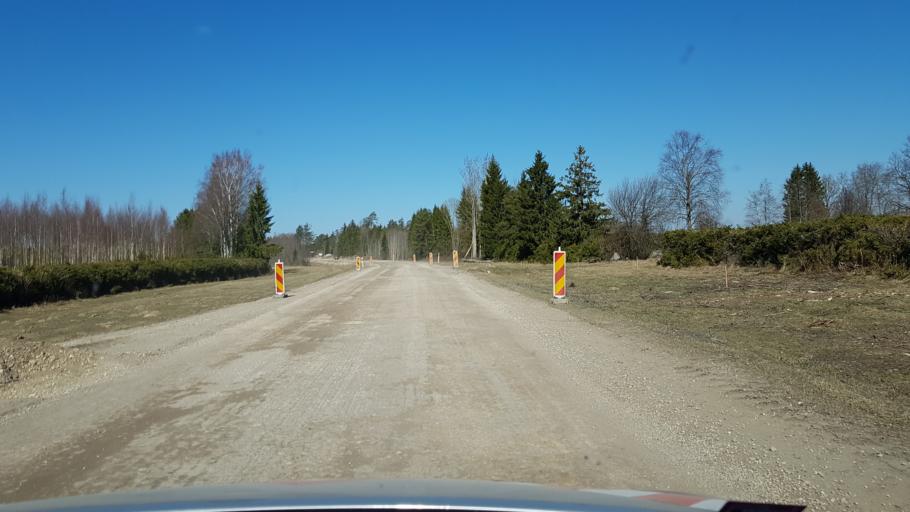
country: EE
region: Laeaene-Virumaa
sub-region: Vinni vald
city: Vinni
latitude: 59.0566
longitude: 26.6494
